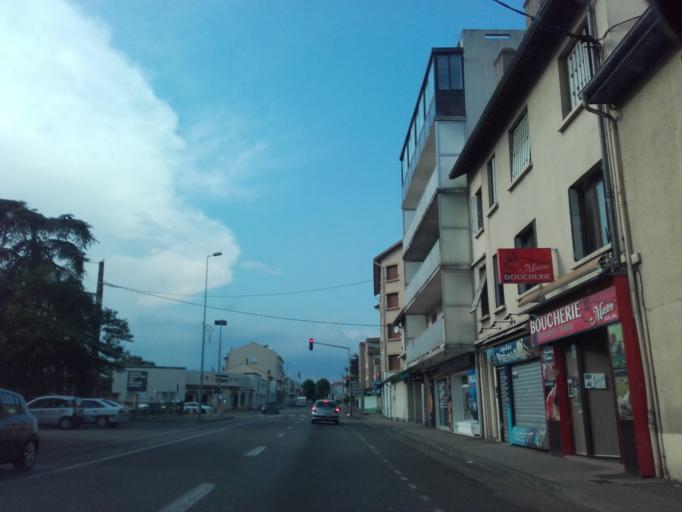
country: FR
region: Rhone-Alpes
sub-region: Departement de l'Isere
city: Le Peage-de-Roussillon
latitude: 45.3617
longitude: 4.8009
